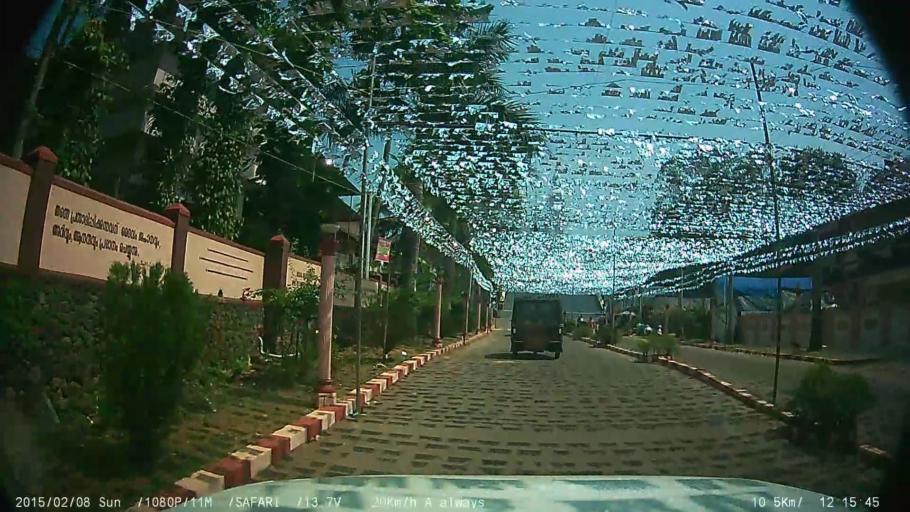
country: IN
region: Kerala
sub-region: Kottayam
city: Palackattumala
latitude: 9.7542
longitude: 76.5629
